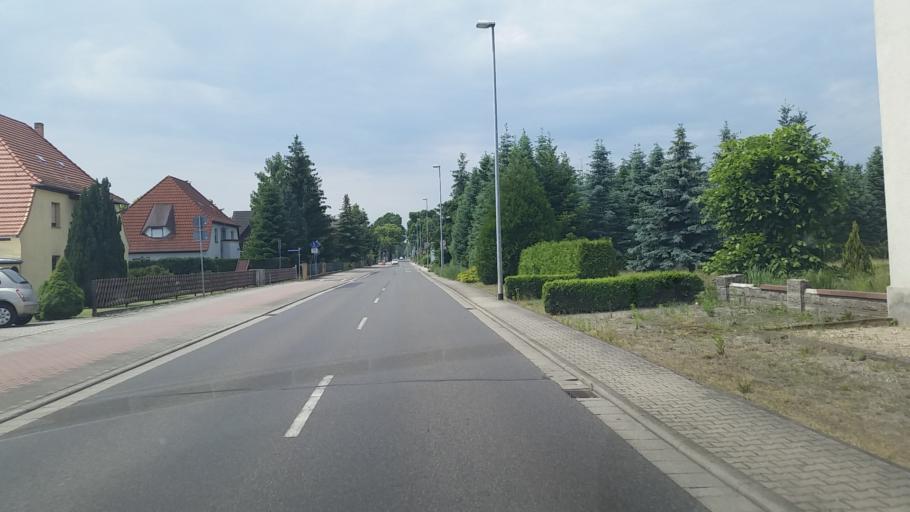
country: DE
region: Brandenburg
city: Schwarzheide
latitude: 51.4888
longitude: 13.8296
